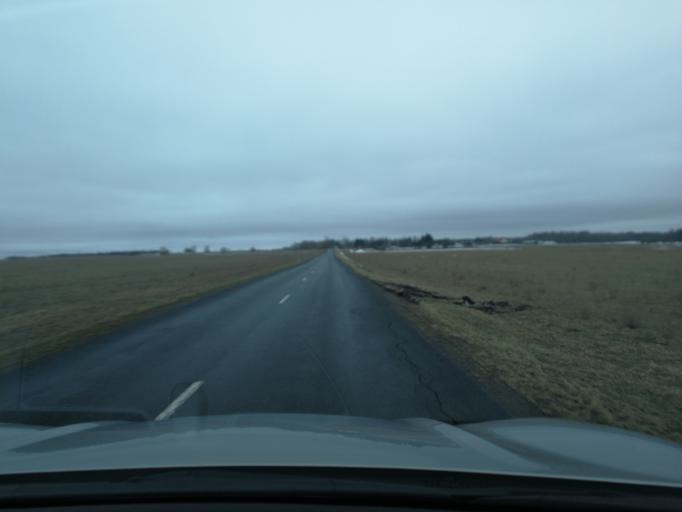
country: EE
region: Harju
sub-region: Kiili vald
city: Kiili
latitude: 59.2828
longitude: 24.8753
